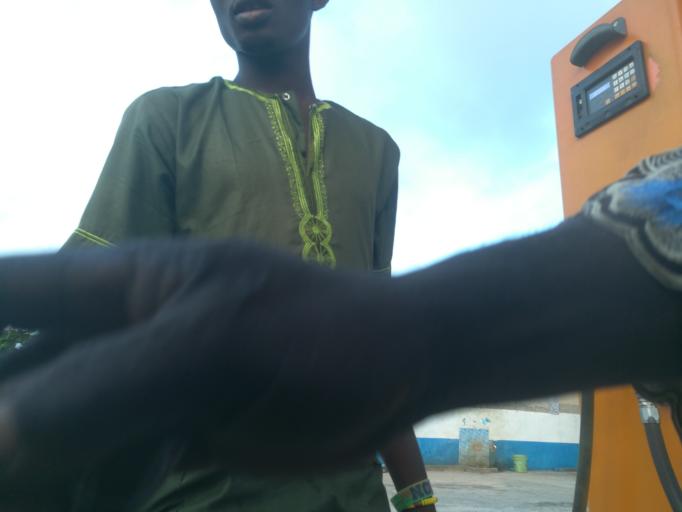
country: NG
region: Ogun
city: Ado Odo
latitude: 6.4788
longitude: 3.0241
